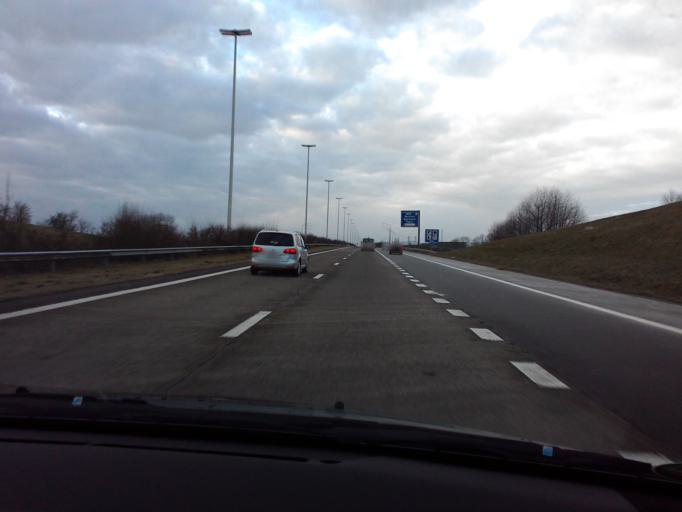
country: BE
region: Wallonia
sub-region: Province de Liege
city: Sprimont
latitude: 50.5058
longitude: 5.6923
